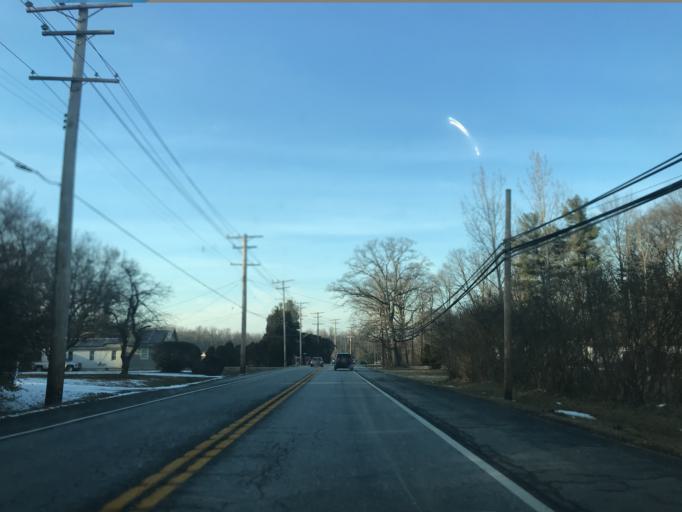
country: US
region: Maryland
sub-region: Harford County
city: Edgewood
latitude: 39.4173
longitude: -76.3280
